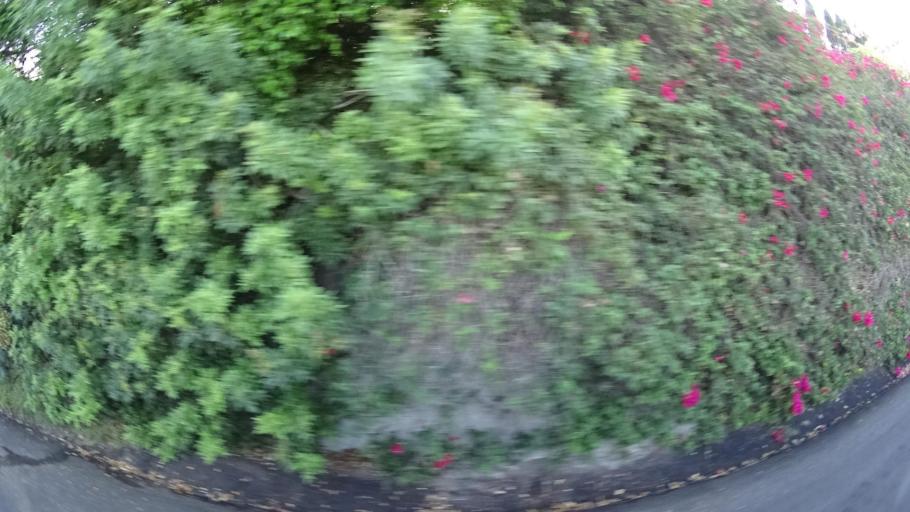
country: US
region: California
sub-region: San Diego County
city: Casa de Oro-Mount Helix
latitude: 32.7671
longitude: -116.9871
